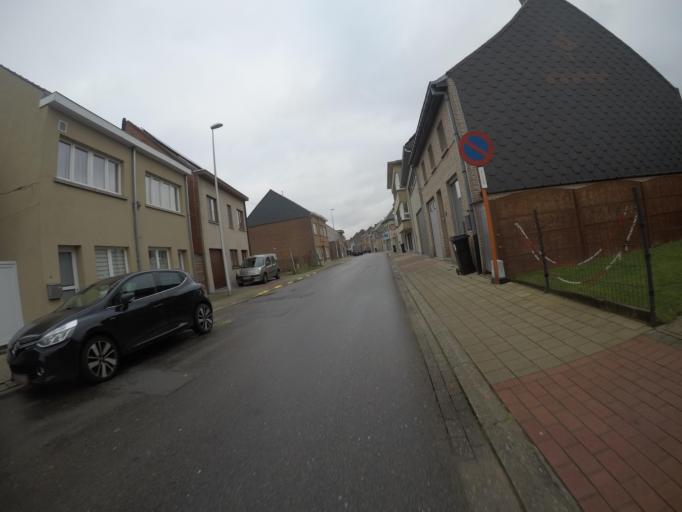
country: BE
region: Flanders
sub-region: Provincie Vlaams-Brabant
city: Liedekerke
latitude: 50.8760
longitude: 4.0878
